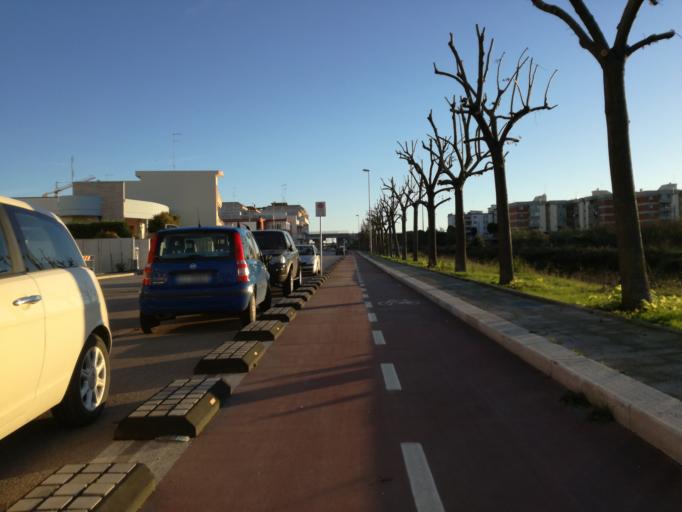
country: IT
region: Apulia
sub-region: Provincia di Bari
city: Adelfia
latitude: 41.0009
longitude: 16.8735
